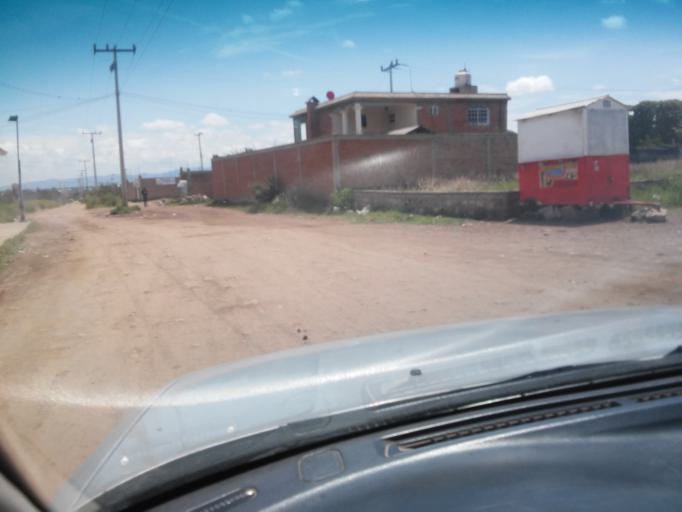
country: MX
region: Durango
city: Victoria de Durango
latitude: 23.9839
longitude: -104.7043
